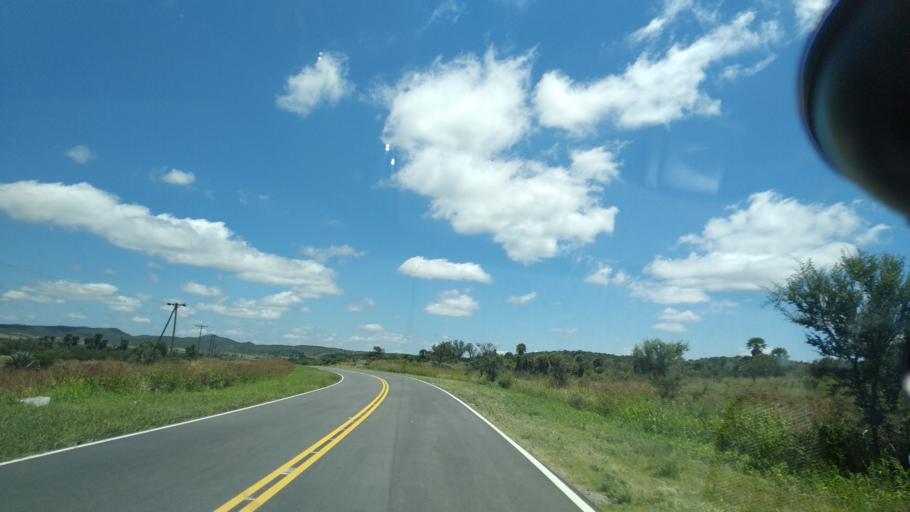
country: AR
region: Cordoba
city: Salsacate
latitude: -31.3735
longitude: -65.1021
